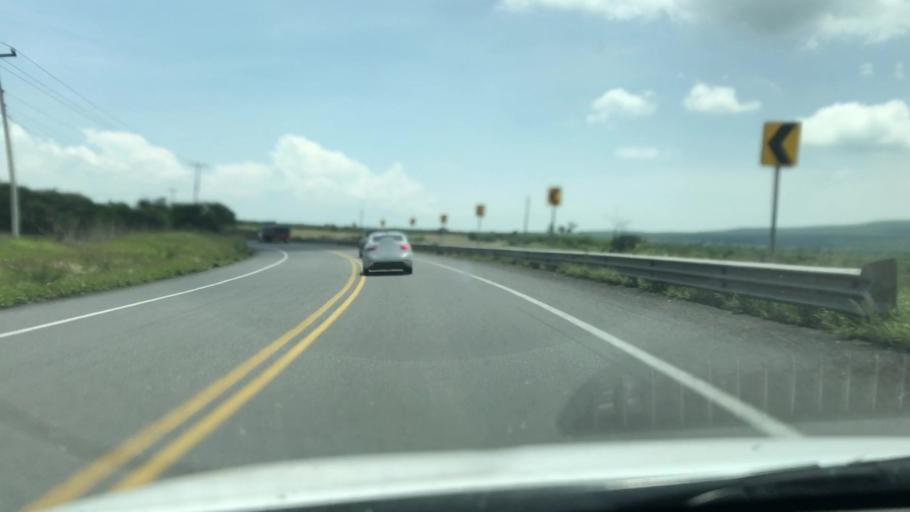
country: MX
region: Michoacan
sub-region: Yurecuaro
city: Yurecuaro
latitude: 20.3425
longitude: -102.1630
